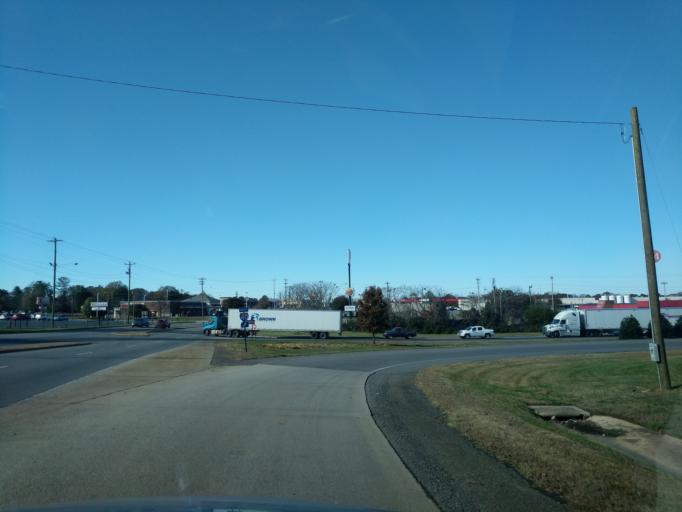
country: US
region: North Carolina
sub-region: Iredell County
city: Statesville
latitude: 35.7944
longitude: -80.9364
